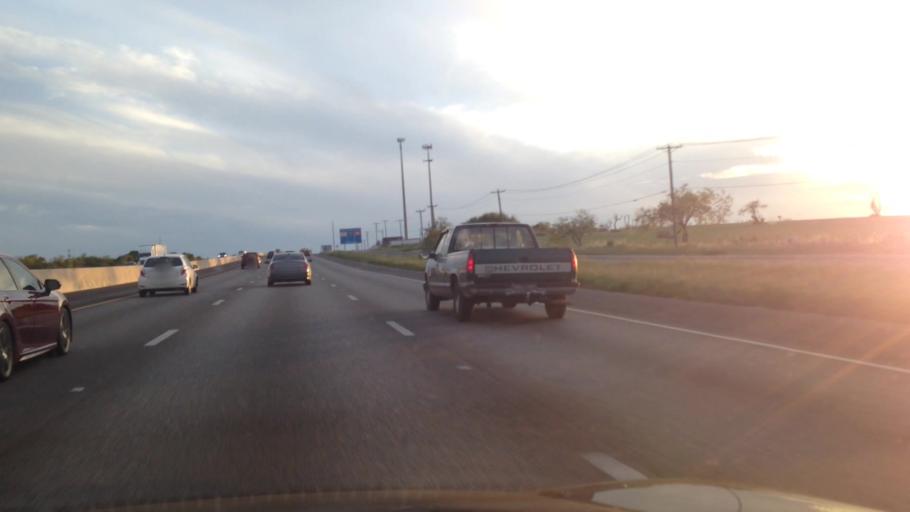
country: US
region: Texas
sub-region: Guadalupe County
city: Lake Dunlap
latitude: 29.7618
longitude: -98.0468
